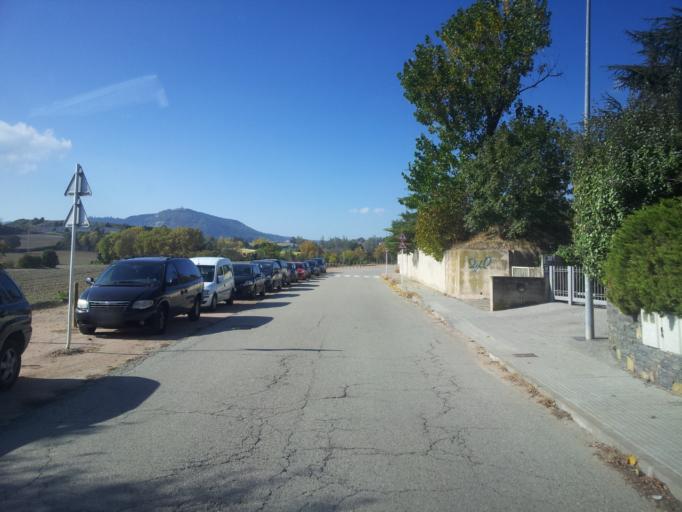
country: ES
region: Catalonia
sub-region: Provincia de Barcelona
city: Vic
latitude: 41.9330
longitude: 2.2374
